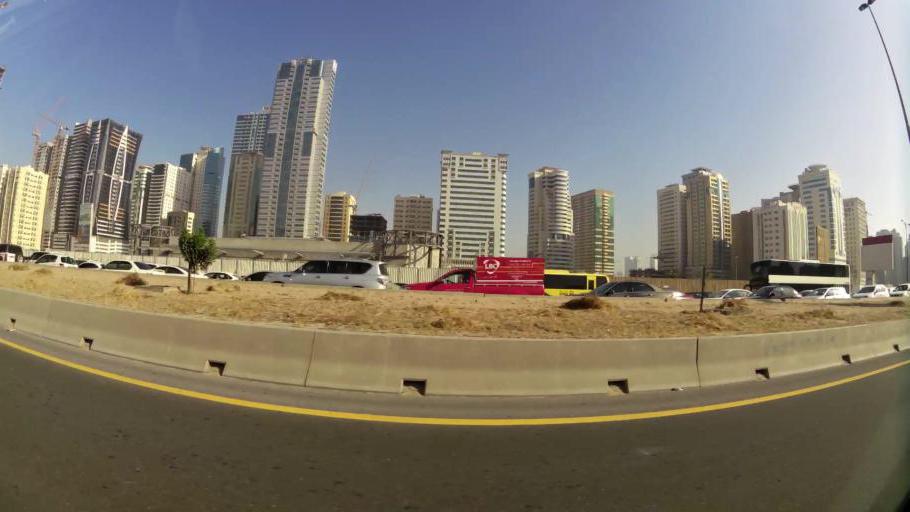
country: AE
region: Ash Shariqah
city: Sharjah
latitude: 25.3049
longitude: 55.3726
